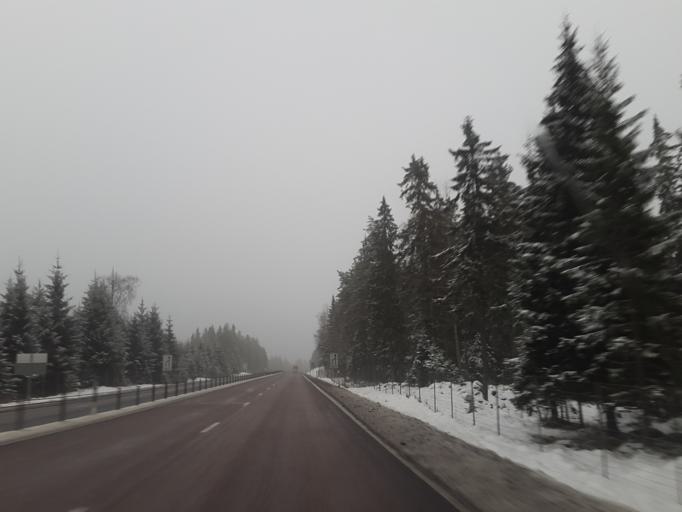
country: SE
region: Joenkoeping
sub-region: Mullsjo Kommun
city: Mullsjoe
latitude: 57.7546
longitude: 13.9239
